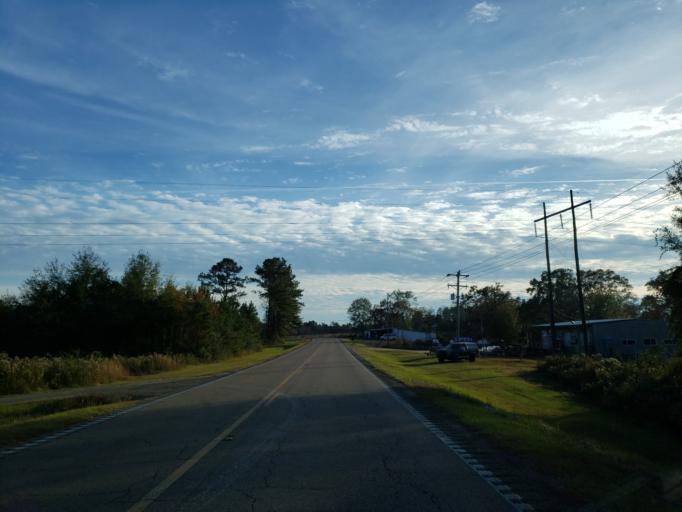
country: US
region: Mississippi
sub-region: Lamar County
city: West Hattiesburg
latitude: 31.2720
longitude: -89.4662
